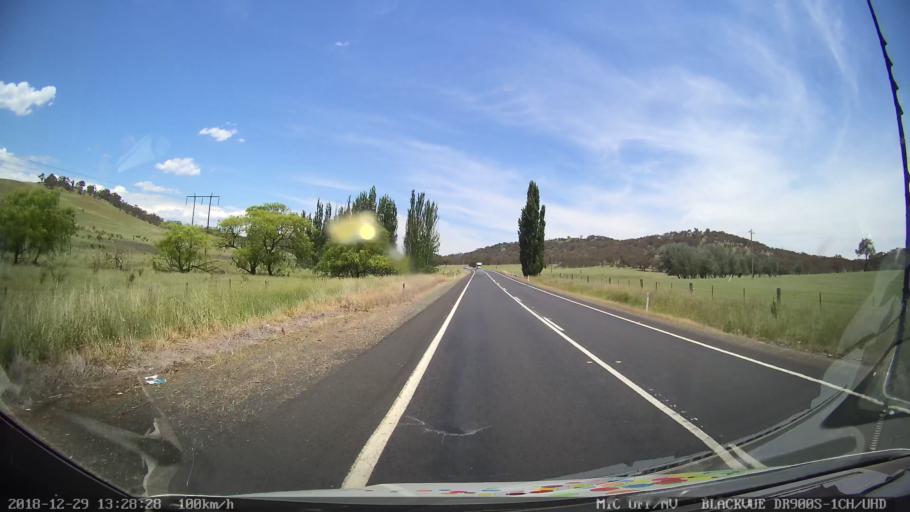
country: AU
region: New South Wales
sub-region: Cooma-Monaro
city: Cooma
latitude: -35.8763
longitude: 149.1610
